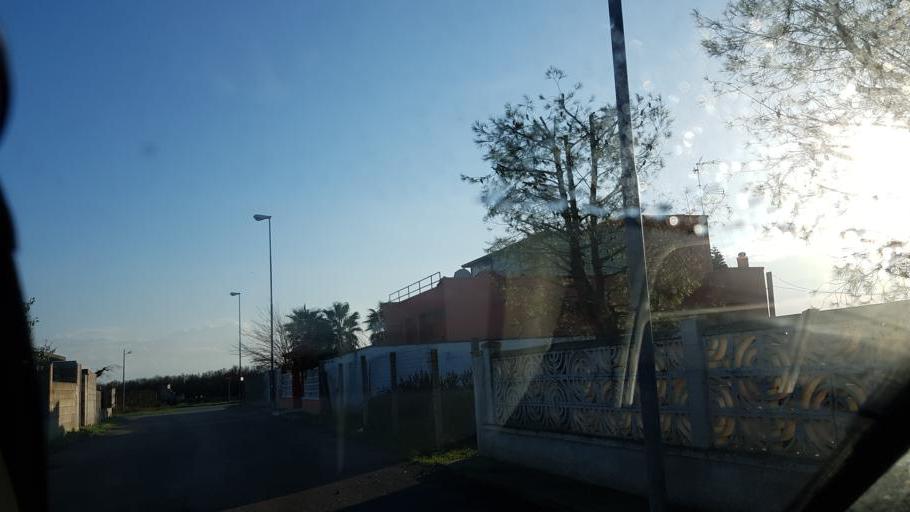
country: IT
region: Apulia
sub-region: Provincia di Brindisi
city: Torchiarolo
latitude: 40.5090
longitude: 18.0918
